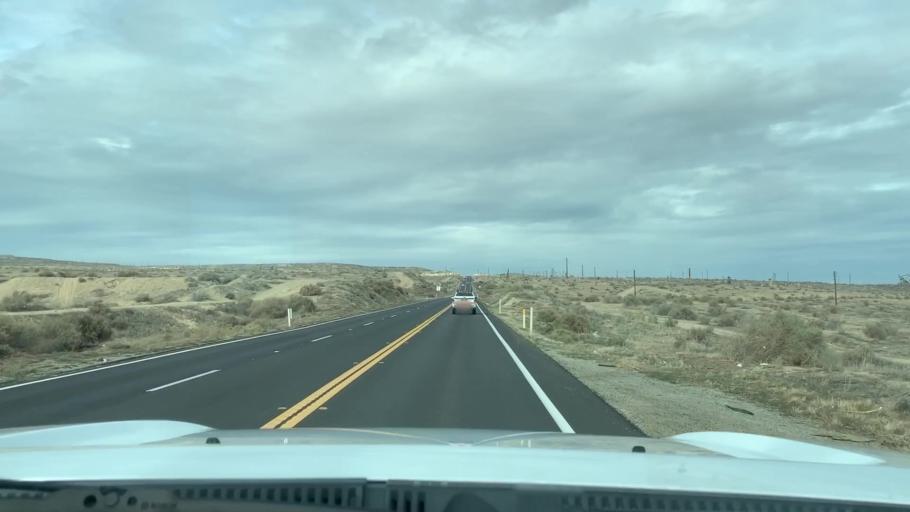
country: US
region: California
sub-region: Kern County
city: South Taft
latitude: 35.1083
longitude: -119.4229
